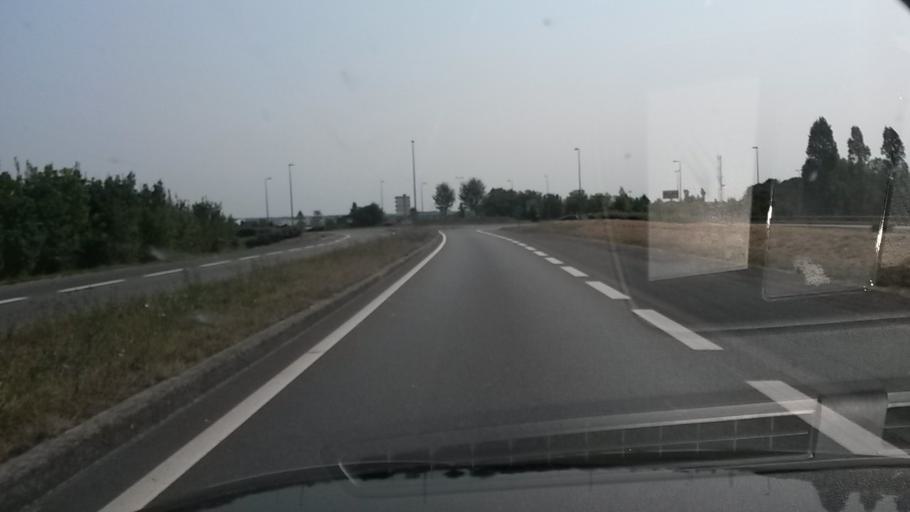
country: FR
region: Pays de la Loire
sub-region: Departement de la Loire-Atlantique
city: Saint-Gereon
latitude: 47.4040
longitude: -1.1911
